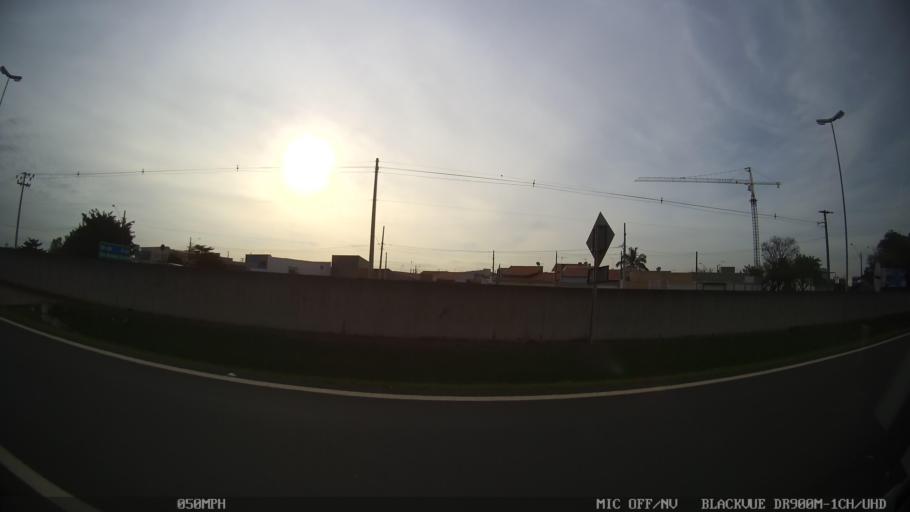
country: BR
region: Sao Paulo
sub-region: Limeira
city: Limeira
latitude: -22.5726
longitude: -47.4460
